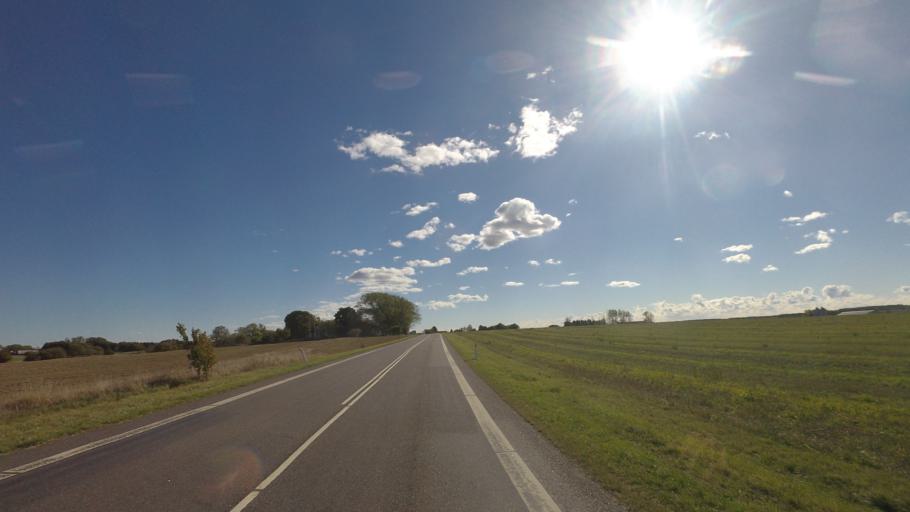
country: DK
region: Capital Region
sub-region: Bornholm Kommune
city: Akirkeby
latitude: 55.1498
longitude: 15.0033
